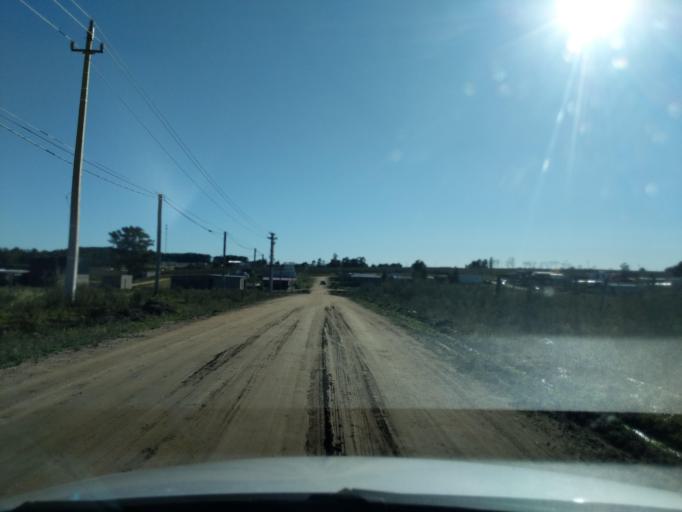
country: UY
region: Florida
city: Florida
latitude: -34.0830
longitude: -56.2386
